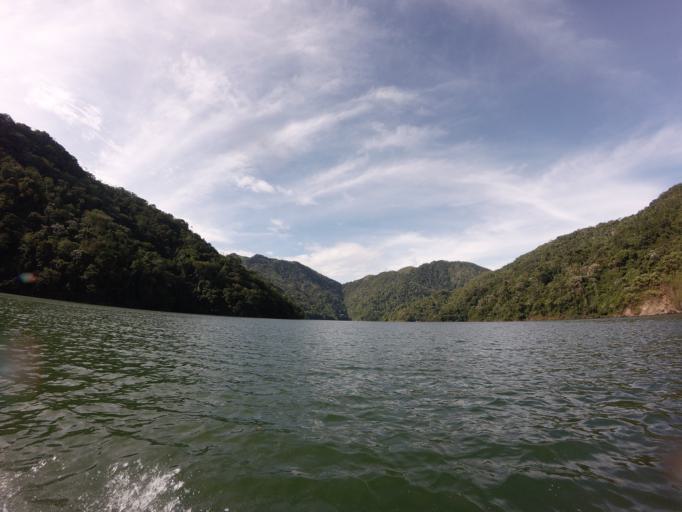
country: CO
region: Caldas
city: Norcasia
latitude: 5.5554
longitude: -74.9104
